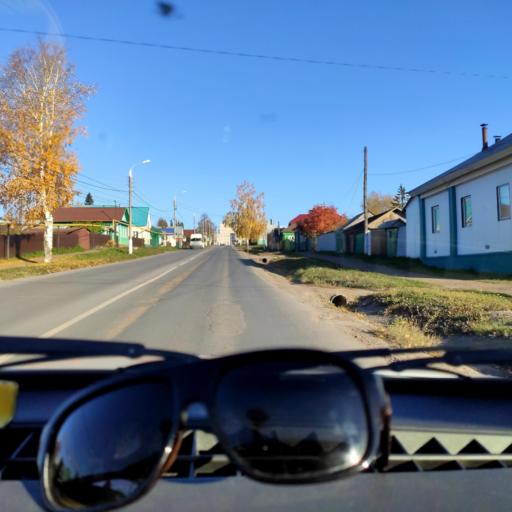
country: RU
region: Bashkortostan
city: Blagoveshchensk
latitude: 55.0424
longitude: 55.9609
